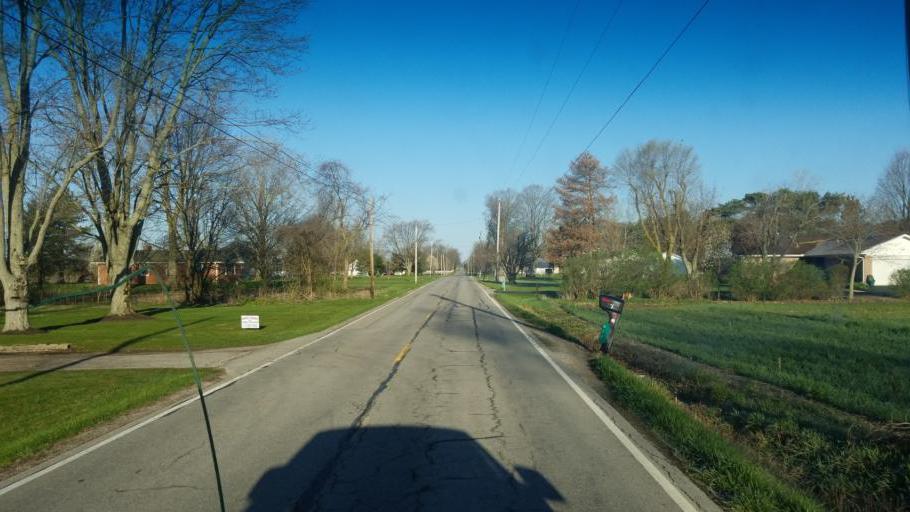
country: US
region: Ohio
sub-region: Marion County
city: Marion
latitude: 40.5348
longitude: -83.1259
